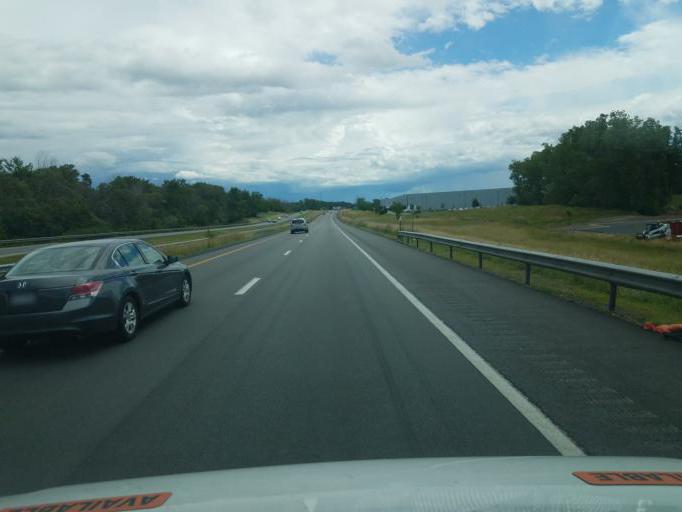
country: US
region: New York
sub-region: Monroe County
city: Scottsville
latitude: 43.0451
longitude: -77.6780
